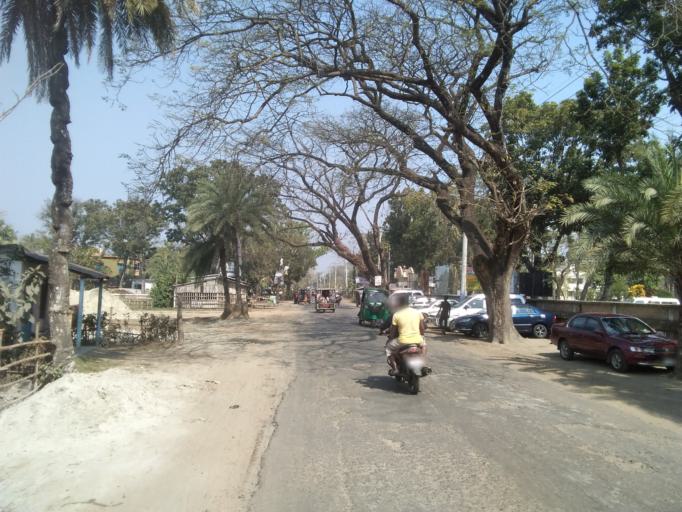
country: IN
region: West Bengal
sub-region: North 24 Parganas
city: Taki
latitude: 22.5908
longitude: 89.0001
